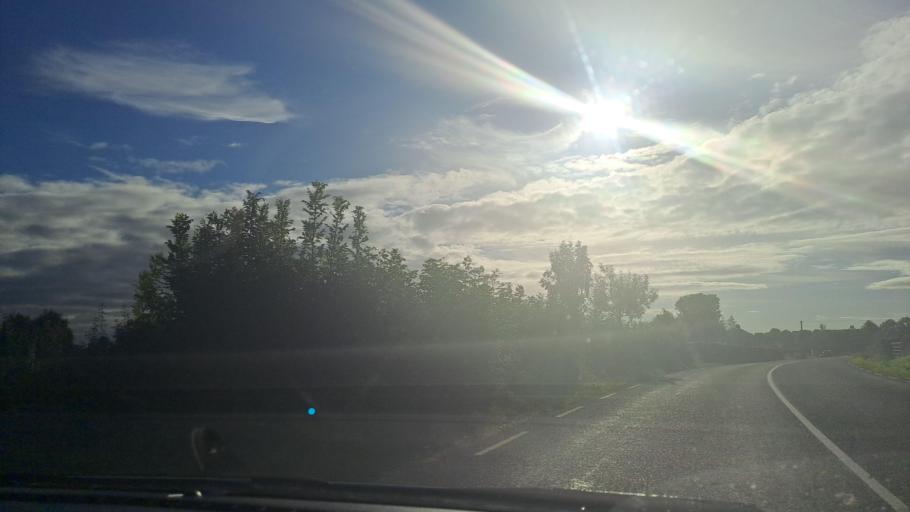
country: IE
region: Ulster
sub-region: County Monaghan
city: Carrickmacross
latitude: 53.9829
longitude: -6.7435
